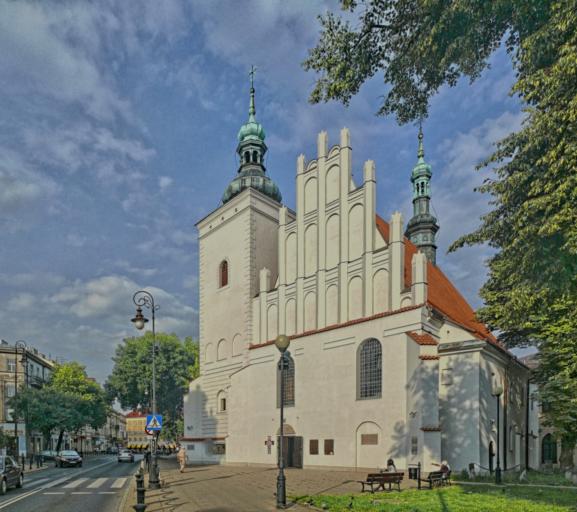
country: PL
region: Lublin Voivodeship
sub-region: Powiat lubelski
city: Lublin
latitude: 51.2463
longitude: 22.5614
